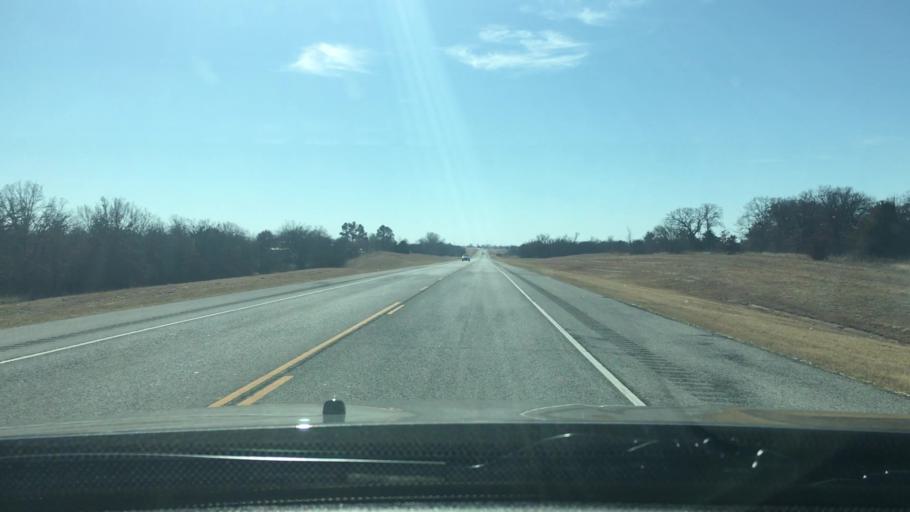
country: US
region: Oklahoma
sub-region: Stephens County
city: Meridian
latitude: 34.4144
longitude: -97.9742
